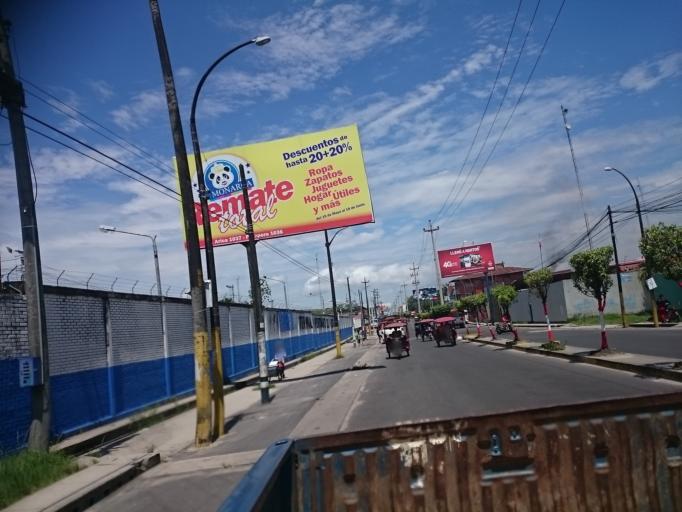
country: PE
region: Loreto
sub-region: Provincia de Maynas
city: Iquitos
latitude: -3.7291
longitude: -73.2406
